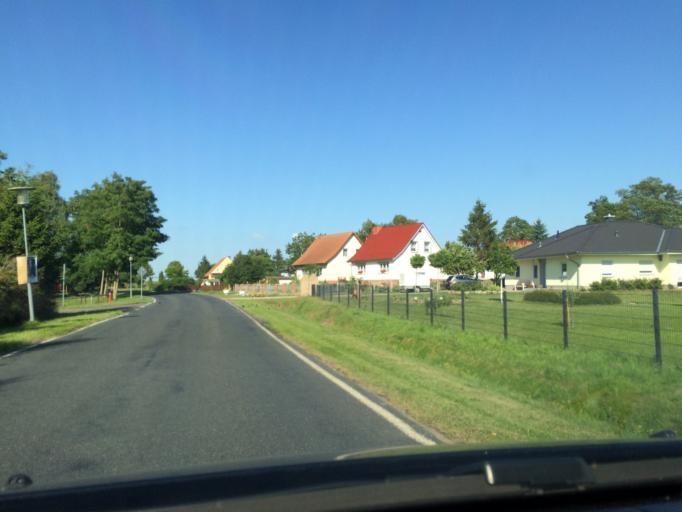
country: DE
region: Mecklenburg-Vorpommern
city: Niepars
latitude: 54.3438
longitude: 12.8932
